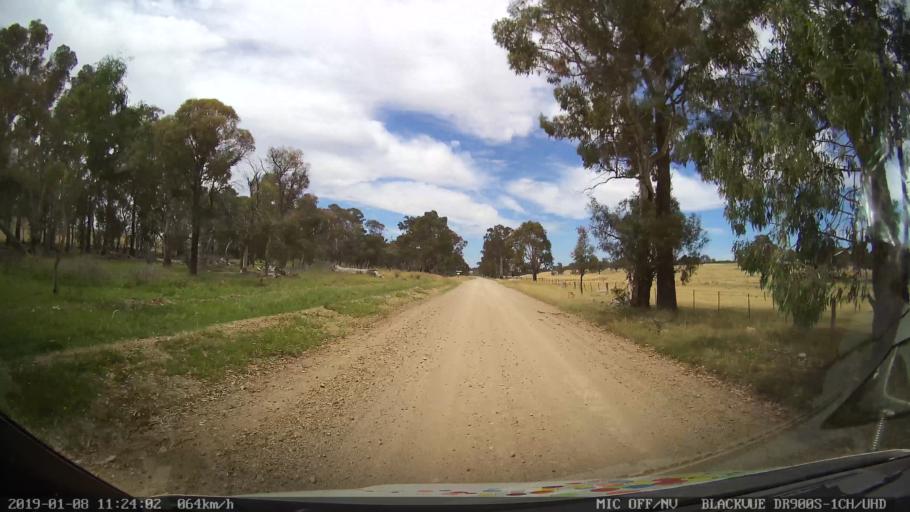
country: AU
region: New South Wales
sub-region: Guyra
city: Guyra
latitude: -30.2608
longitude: 151.5584
